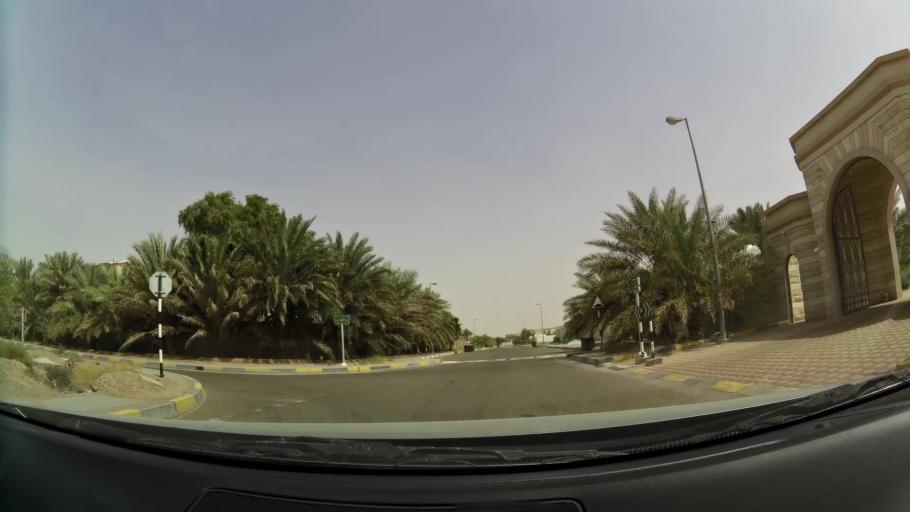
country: AE
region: Abu Dhabi
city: Al Ain
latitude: 24.1661
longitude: 55.6608
